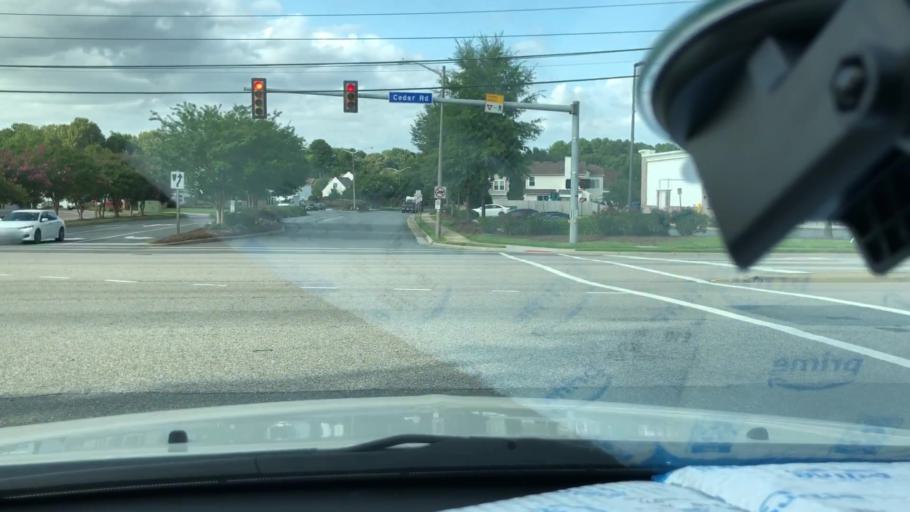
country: US
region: Virginia
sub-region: City of Chesapeake
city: Chesapeake
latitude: 36.7117
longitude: -76.2771
